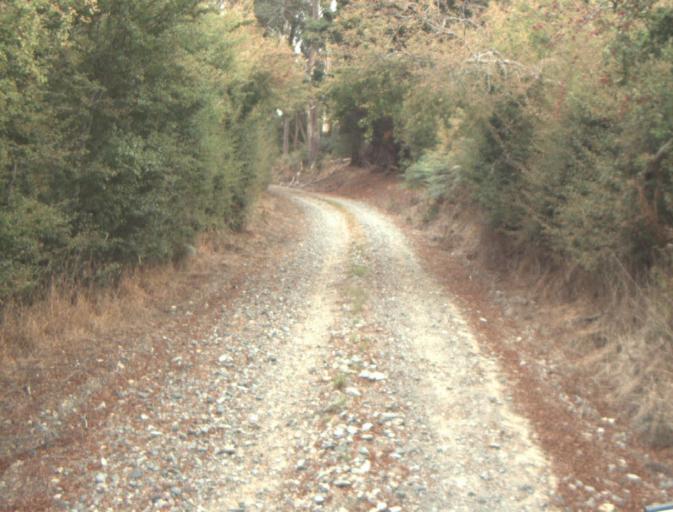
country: AU
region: Tasmania
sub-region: Launceston
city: Mayfield
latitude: -41.2486
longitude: 147.2005
